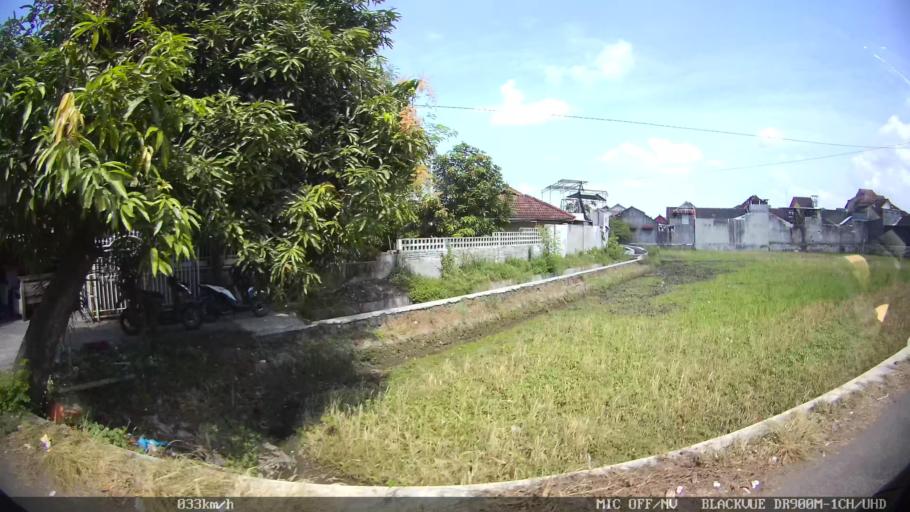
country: ID
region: Daerah Istimewa Yogyakarta
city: Yogyakarta
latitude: -7.8287
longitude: 110.3797
